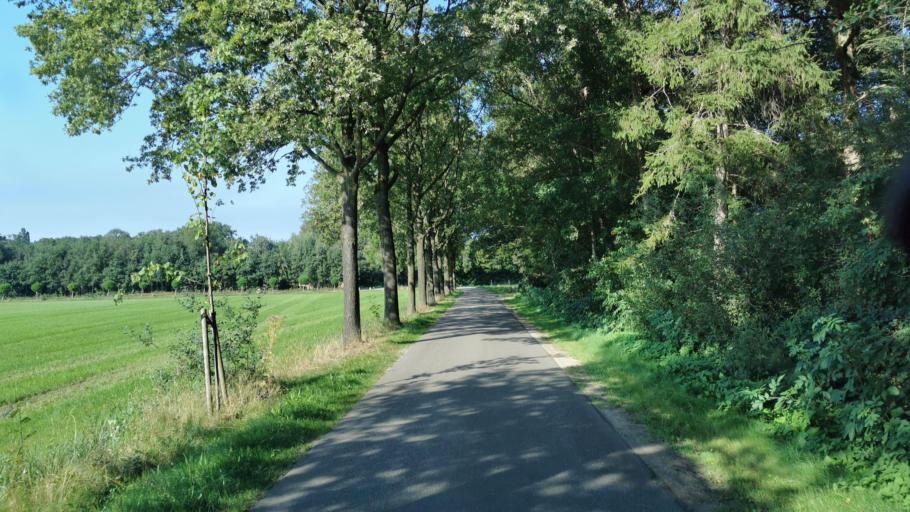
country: DE
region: Lower Saxony
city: Lage
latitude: 52.4153
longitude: 6.9486
